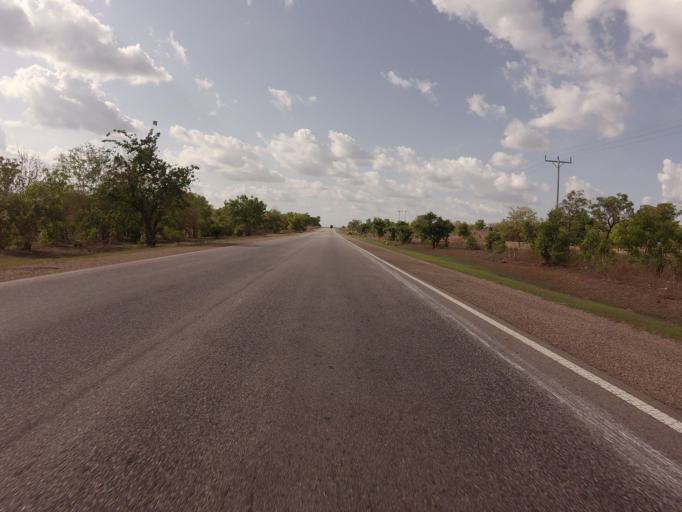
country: GH
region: Upper East
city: Bolgatanga
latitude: 10.5678
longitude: -0.8335
